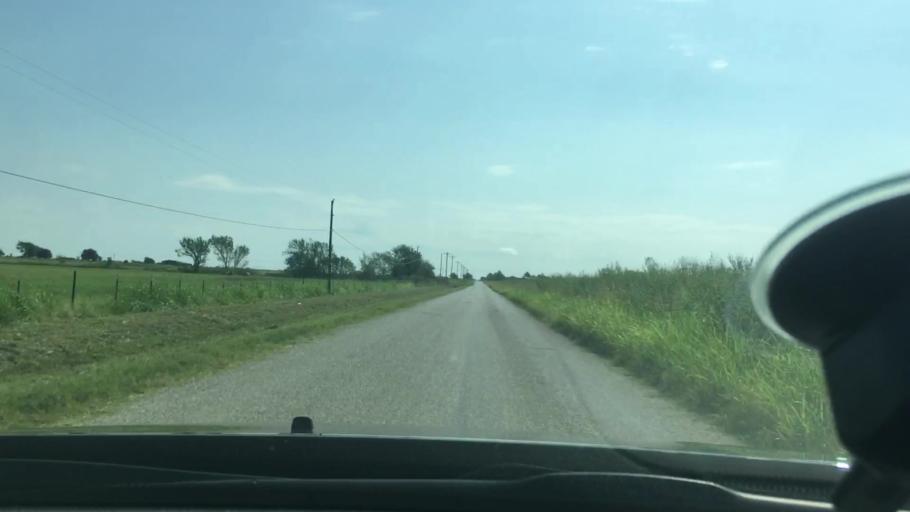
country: US
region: Oklahoma
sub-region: Bryan County
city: Colbert
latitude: 33.9110
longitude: -96.5080
